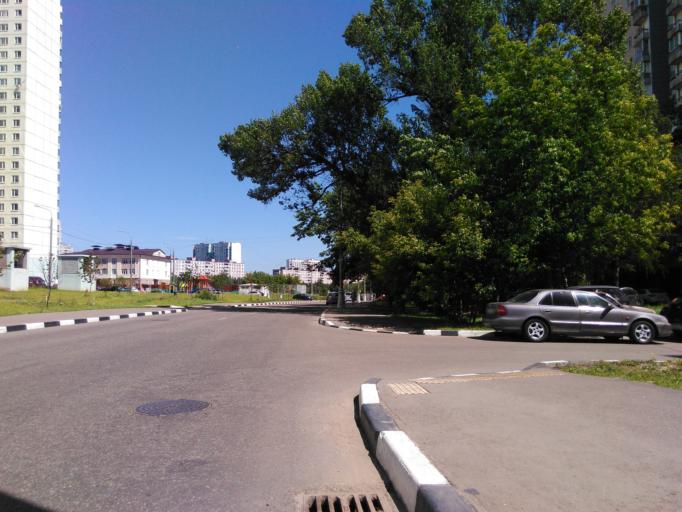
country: RU
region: Moskovskaya
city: Cheremushki
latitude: 55.6627
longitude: 37.5669
